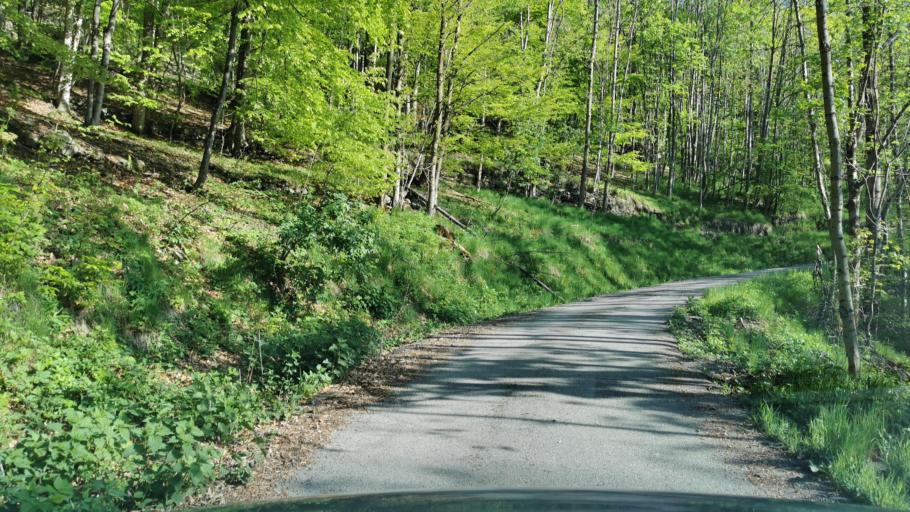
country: IT
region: Piedmont
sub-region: Provincia di Torino
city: Lemie
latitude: 45.2336
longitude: 7.2851
